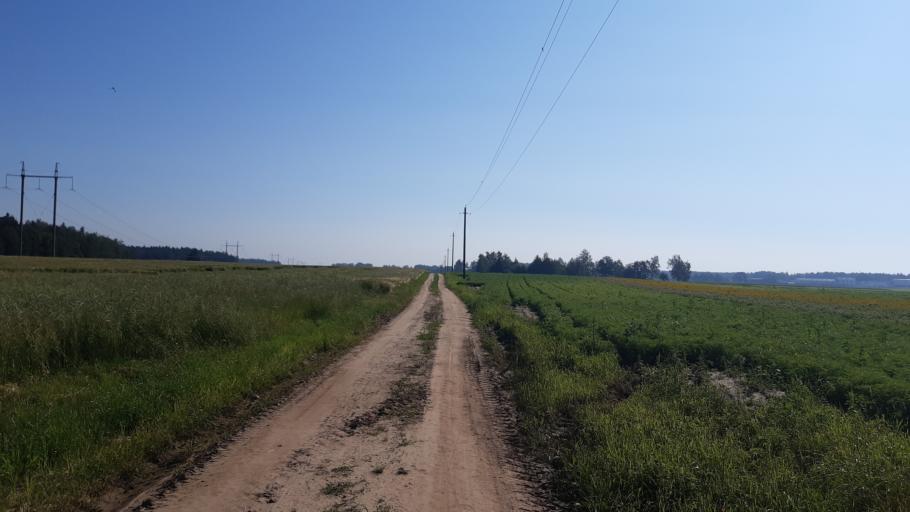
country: BY
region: Minsk
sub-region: Smalyavitski Rayon
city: Oktjabr'skij
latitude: 54.0863
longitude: 28.2192
